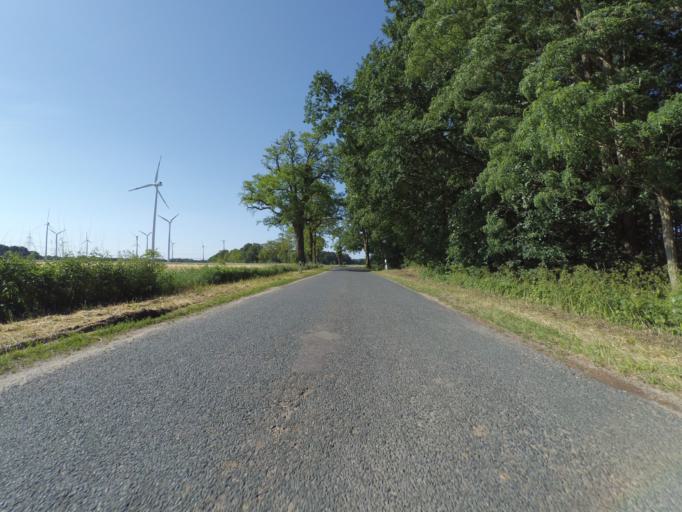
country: DE
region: Brandenburg
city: Triglitz
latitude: 53.2605
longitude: 12.1233
